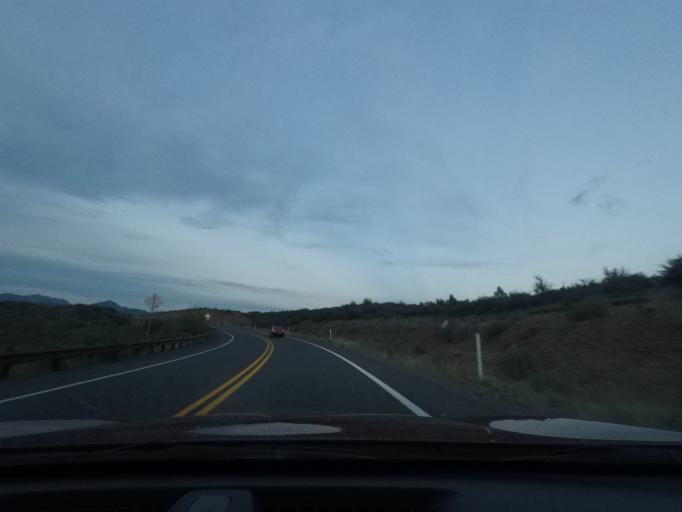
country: US
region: Arizona
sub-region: Yavapai County
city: Williamson
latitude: 34.5647
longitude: -112.6645
